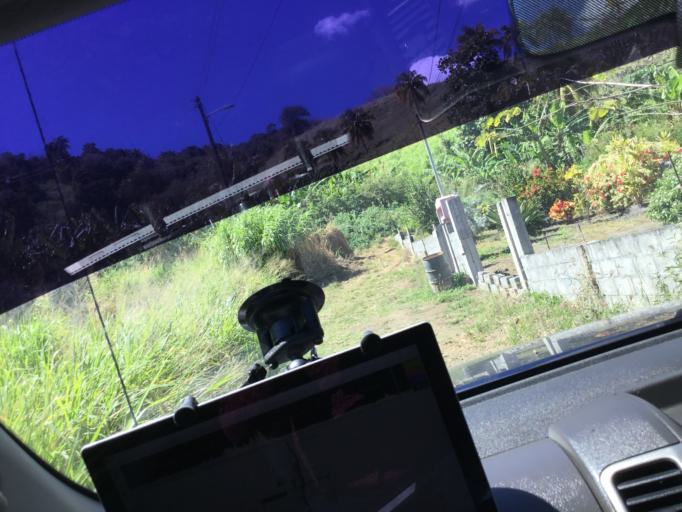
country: VC
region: Charlotte
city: Byera Village
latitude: 13.2653
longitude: -61.1214
